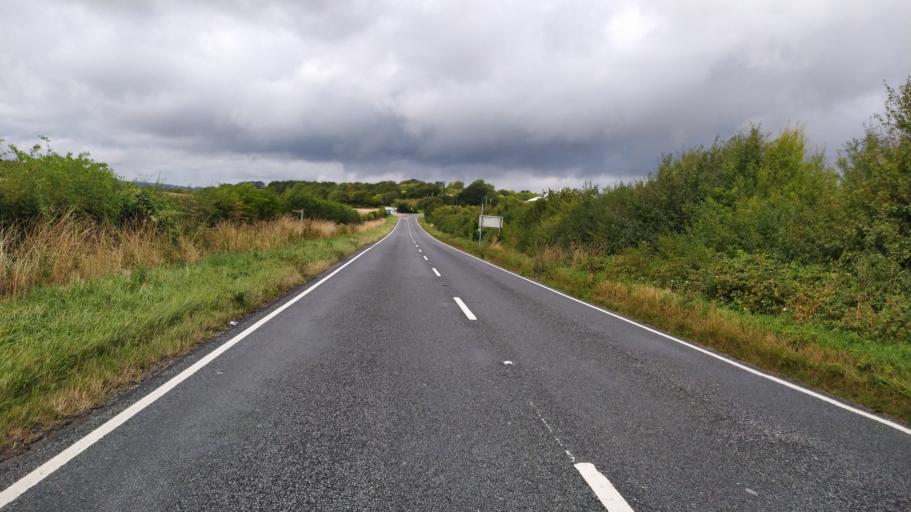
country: GB
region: England
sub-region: Hampshire
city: Kings Worthy
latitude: 51.0557
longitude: -1.2585
